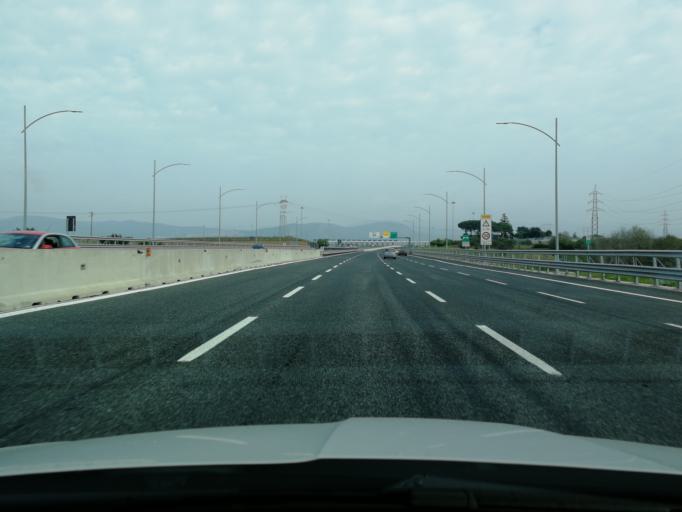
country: IT
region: Latium
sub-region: Citta metropolitana di Roma Capitale
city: Albuccione
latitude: 41.9257
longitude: 12.6964
